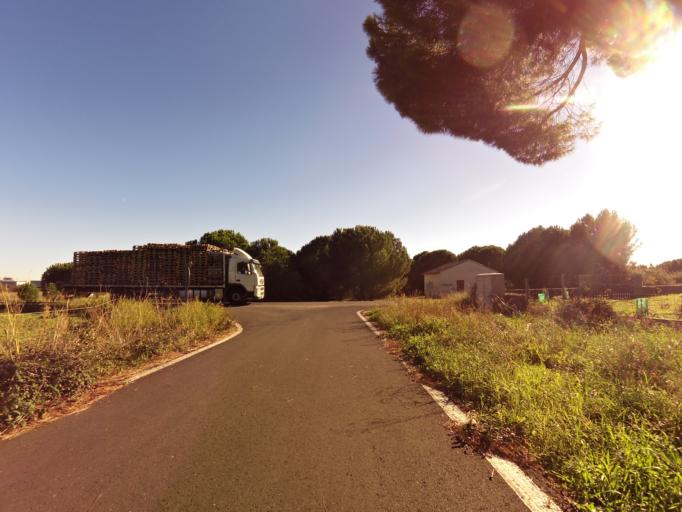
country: FR
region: Languedoc-Roussillon
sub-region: Departement du Gard
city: Aigues-Vives
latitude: 43.7248
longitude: 4.1837
